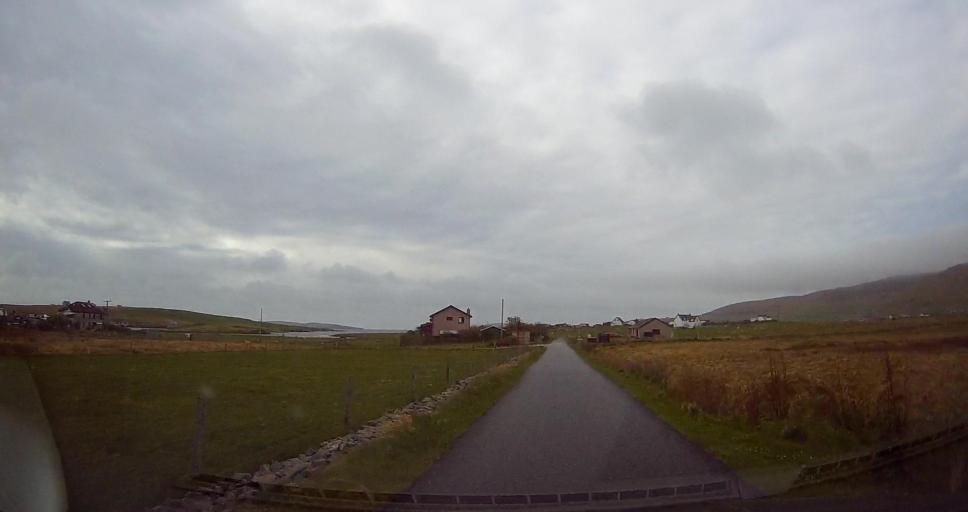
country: GB
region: Scotland
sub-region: Shetland Islands
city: Sandwick
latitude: 60.0455
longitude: -1.2167
